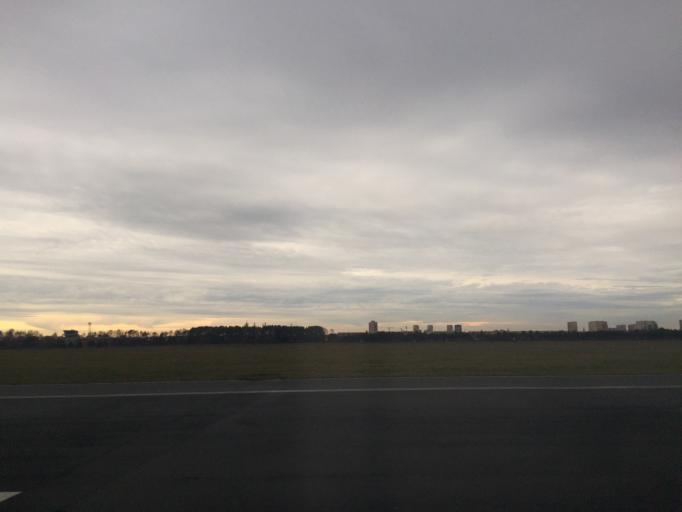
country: PL
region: Kujawsko-Pomorskie
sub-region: Bydgoszcz
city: Bydgoszcz
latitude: 53.0976
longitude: 17.9851
